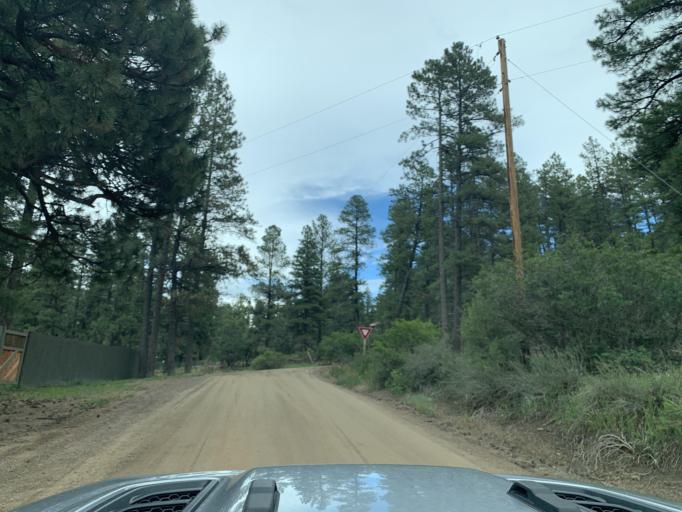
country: US
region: Colorado
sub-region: Archuleta County
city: Pagosa Springs
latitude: 37.2215
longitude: -107.1844
